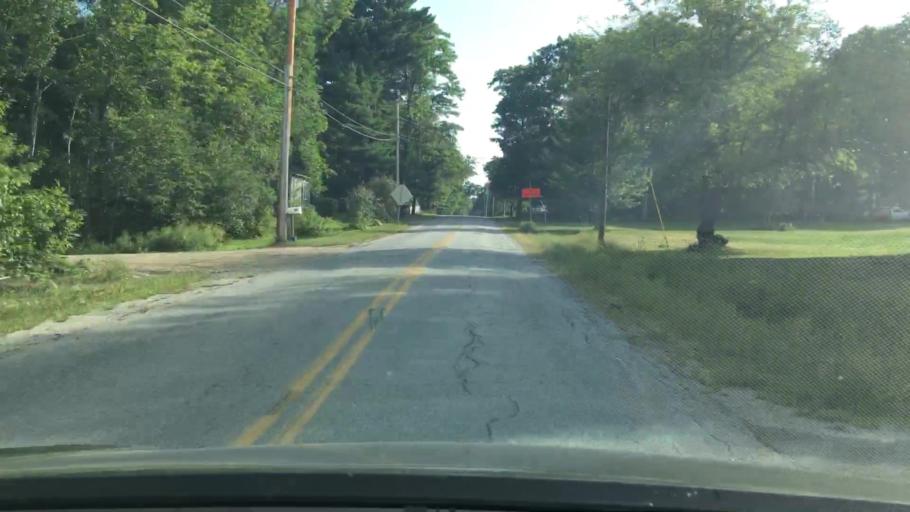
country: US
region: Maine
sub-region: Hancock County
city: Bucksport
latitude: 44.5568
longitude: -68.7942
